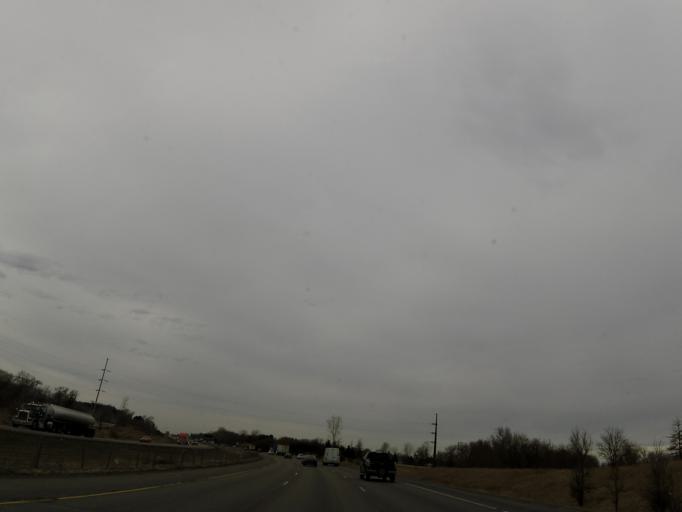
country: US
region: Minnesota
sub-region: Dakota County
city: Mendota Heights
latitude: 44.8624
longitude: -93.1087
